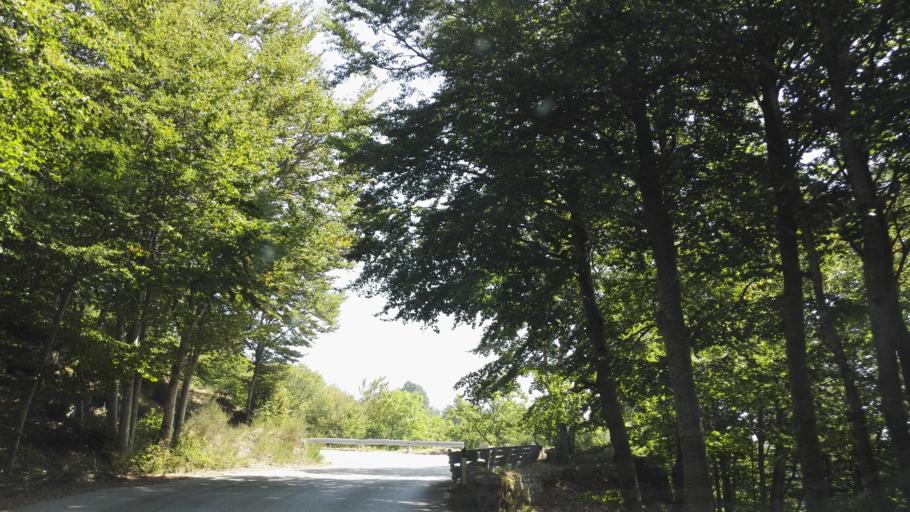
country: IT
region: Calabria
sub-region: Provincia di Vibo-Valentia
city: Nardodipace
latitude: 38.5039
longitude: 16.3526
